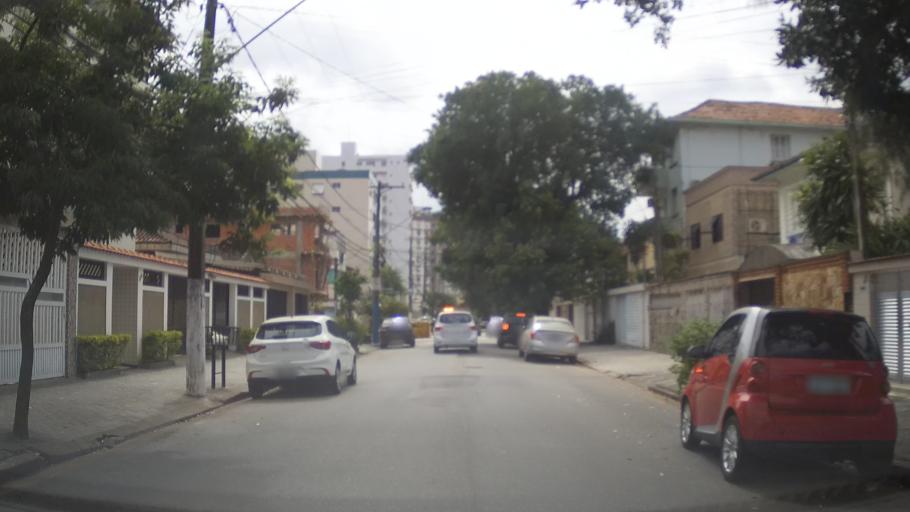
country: BR
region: Sao Paulo
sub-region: Santos
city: Santos
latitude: -23.9604
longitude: -46.3199
